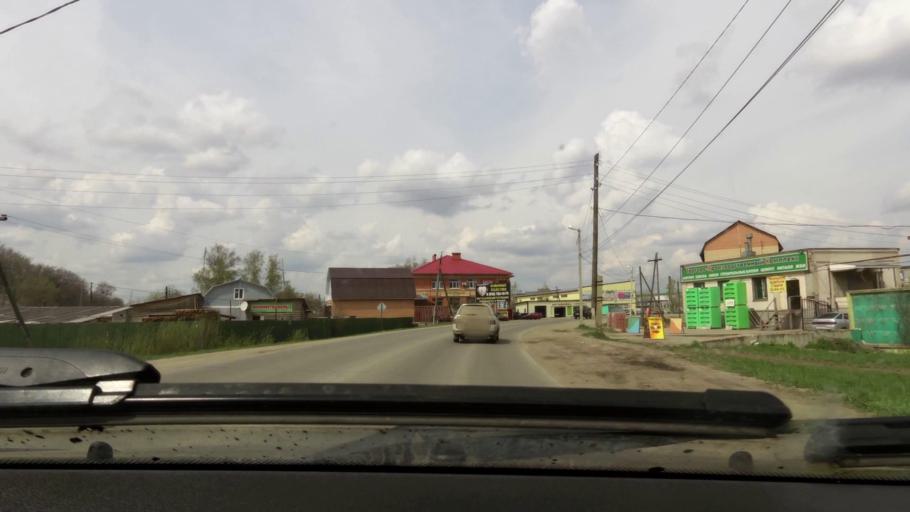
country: RU
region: Rjazan
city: Bagramovo
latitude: 54.7342
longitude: 39.4826
